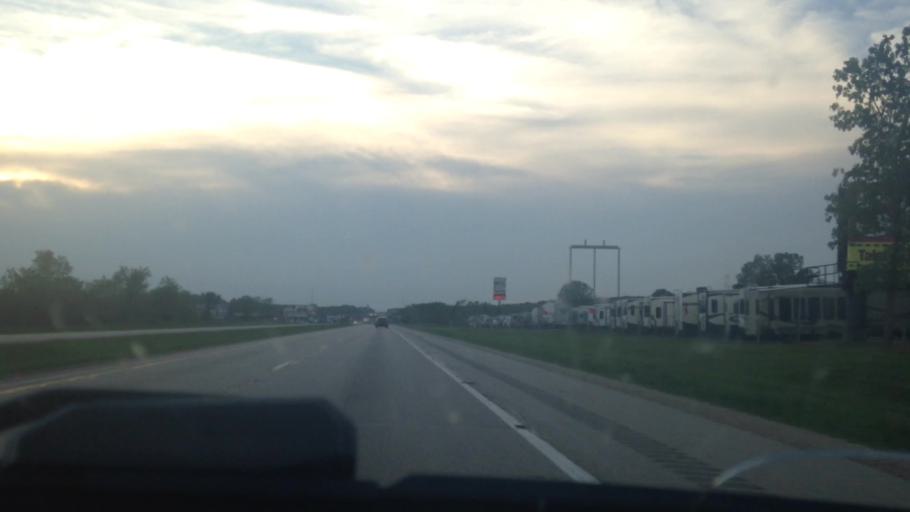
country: US
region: Wisconsin
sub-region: Washington County
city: Richfield
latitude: 43.3035
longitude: -88.2216
